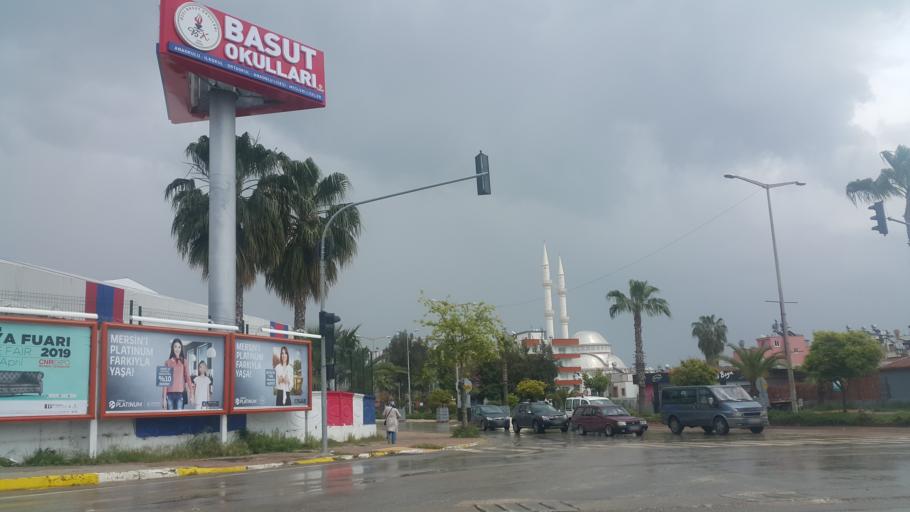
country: TR
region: Mersin
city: Mercin
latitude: 36.8146
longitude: 34.6050
